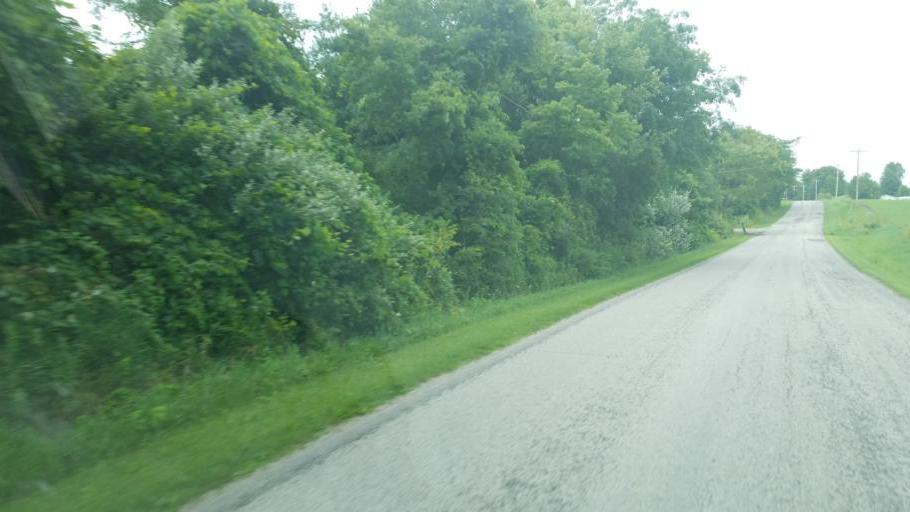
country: US
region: Ohio
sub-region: Delaware County
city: Ashley
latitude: 40.4368
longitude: -82.9751
